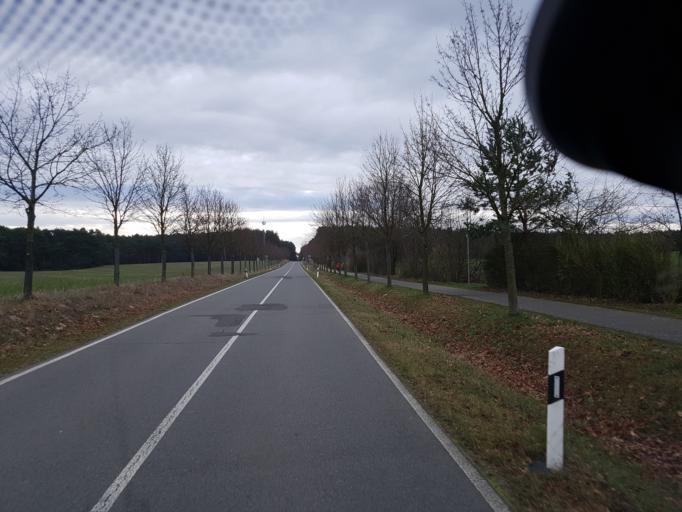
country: DE
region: Brandenburg
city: Mixdorf
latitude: 52.1936
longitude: 14.4141
